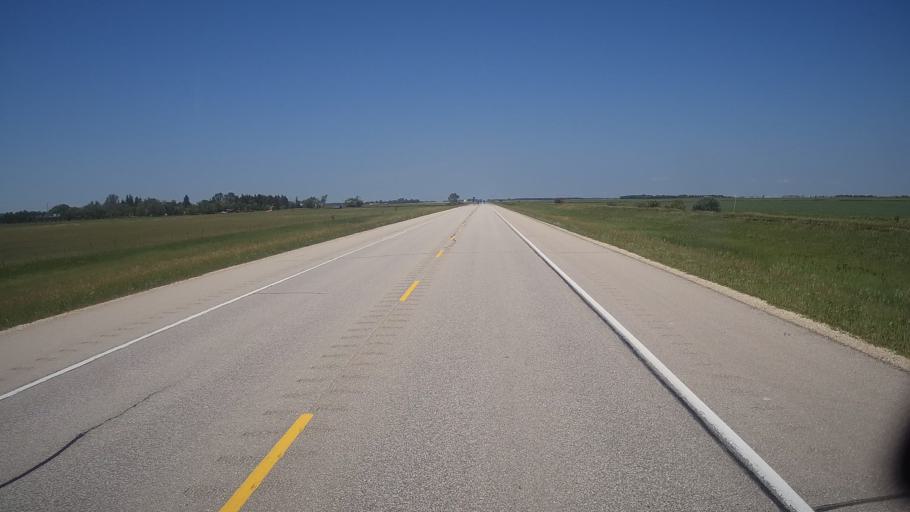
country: CA
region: Manitoba
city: Stonewall
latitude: 50.0162
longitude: -97.3688
